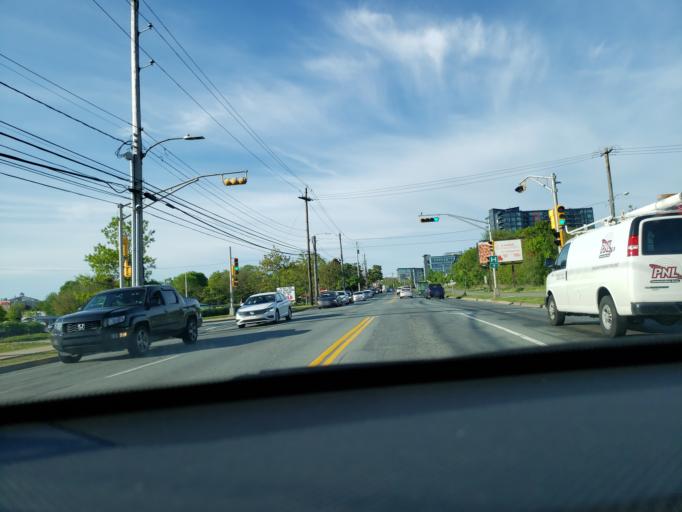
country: CA
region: Nova Scotia
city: Dartmouth
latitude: 44.6583
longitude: -63.6292
